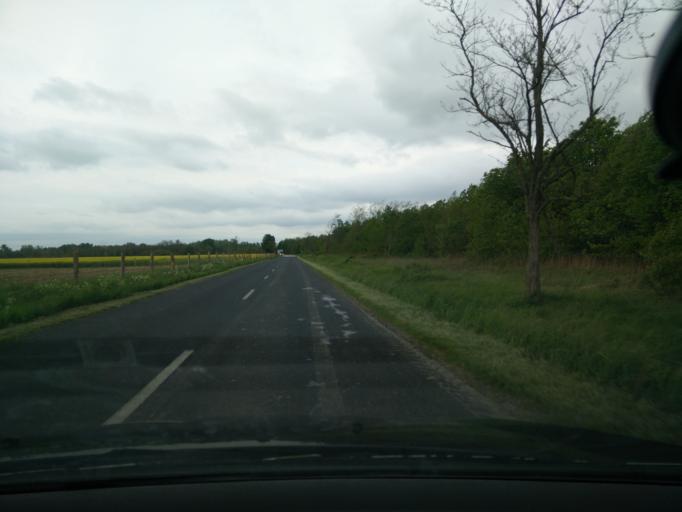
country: HU
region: Veszprem
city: Papa
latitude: 47.2446
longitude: 17.3872
